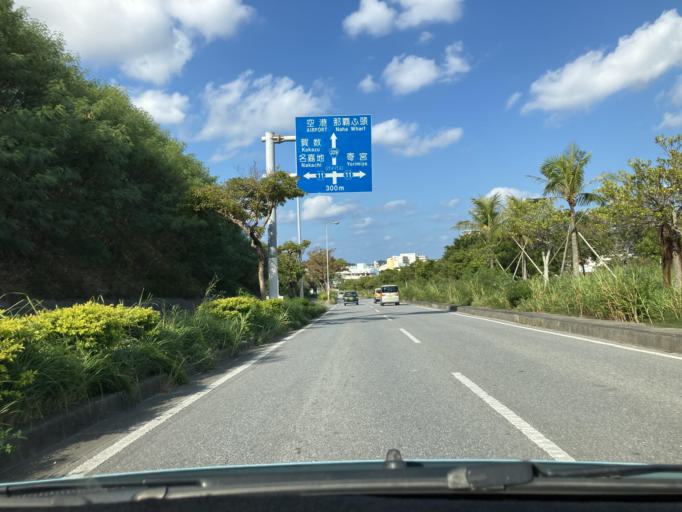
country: JP
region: Okinawa
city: Tomigusuku
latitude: 26.1932
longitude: 127.6985
